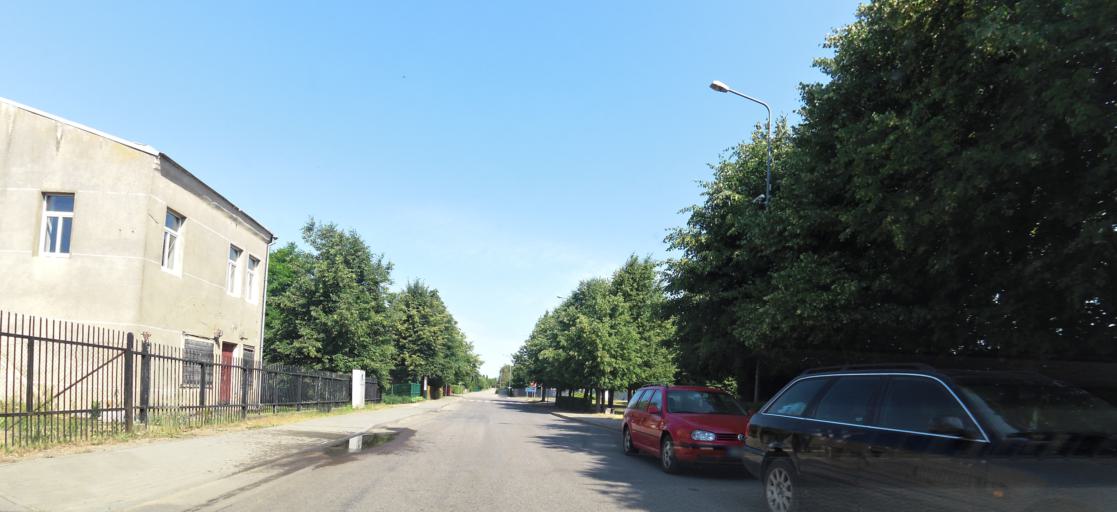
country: LT
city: Grigiskes
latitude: 54.8699
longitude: 25.0637
